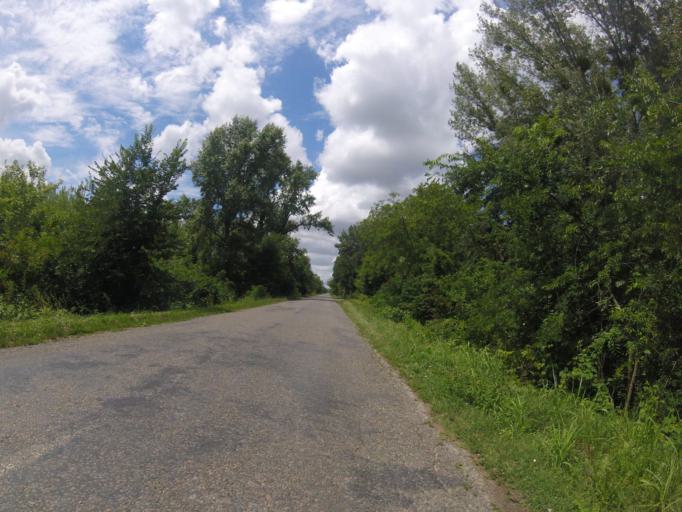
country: HU
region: Tolna
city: Bogyiszlo
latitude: 46.3301
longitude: 18.8371
